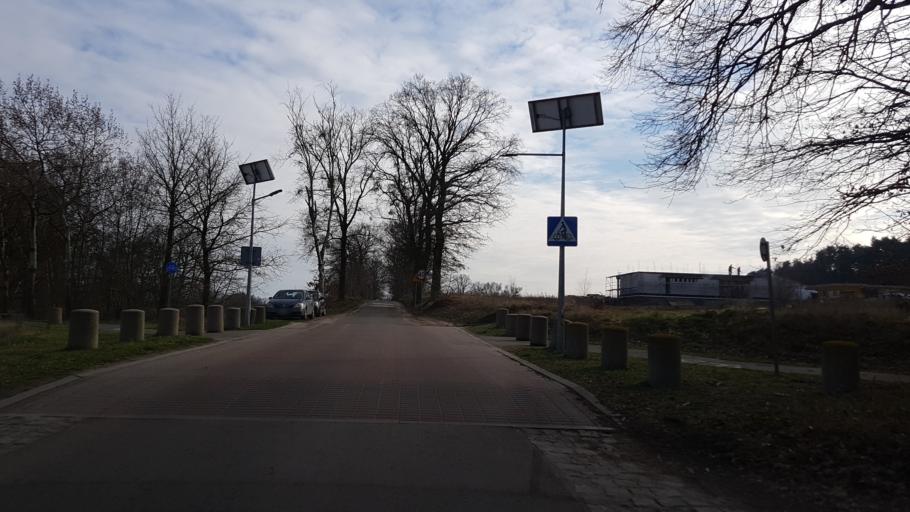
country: PL
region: West Pomeranian Voivodeship
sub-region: Powiat policki
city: Dobra
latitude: 53.5126
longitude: 14.3497
